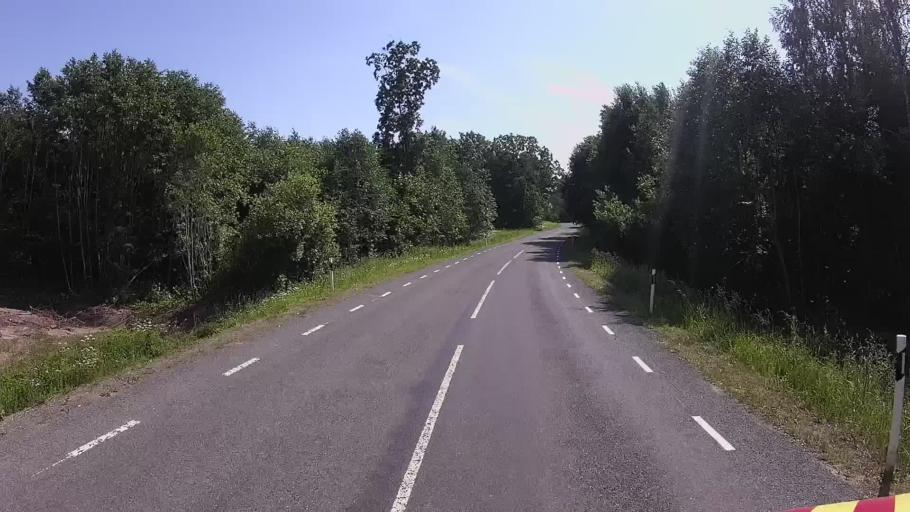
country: EE
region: Viljandimaa
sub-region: Karksi vald
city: Karksi-Nuia
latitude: 58.0435
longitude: 25.5455
